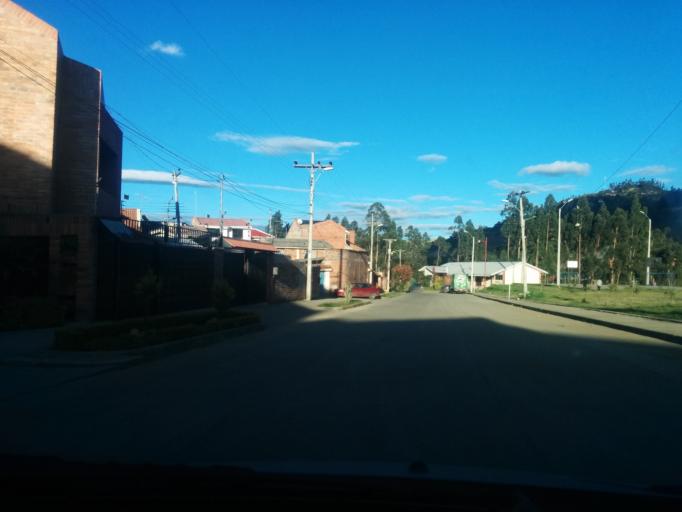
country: EC
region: Azuay
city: Cuenca
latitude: -2.8927
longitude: -78.9665
